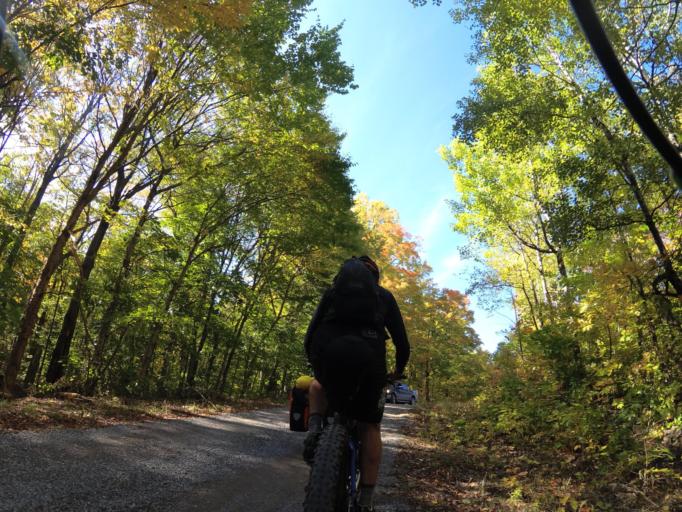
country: CA
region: Ontario
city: Renfrew
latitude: 45.3441
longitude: -77.0931
